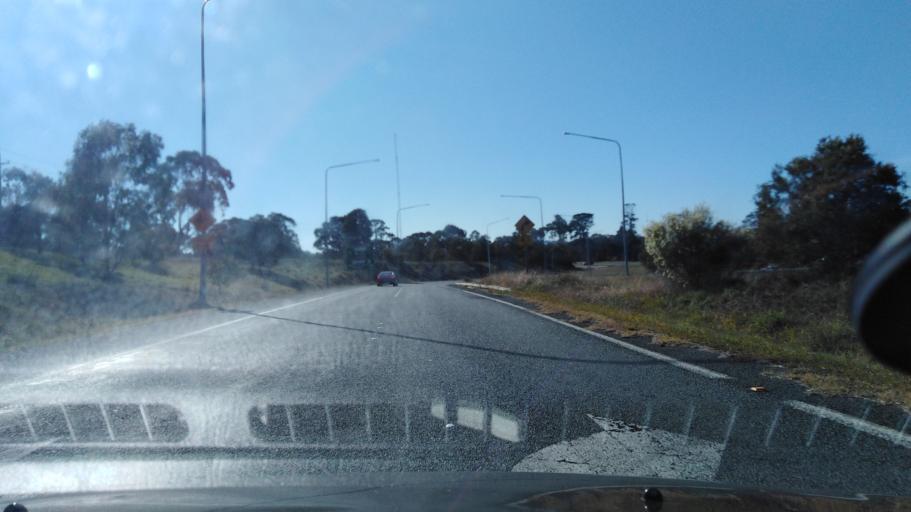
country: AU
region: Australian Capital Territory
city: Kaleen
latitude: -35.2257
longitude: 149.1199
